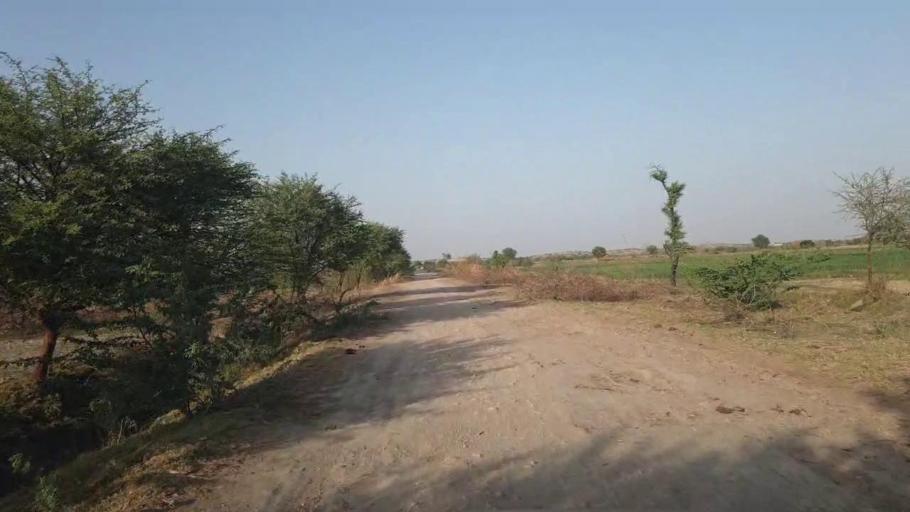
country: PK
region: Sindh
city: Dhoro Naro
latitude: 25.4957
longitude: 69.5832
